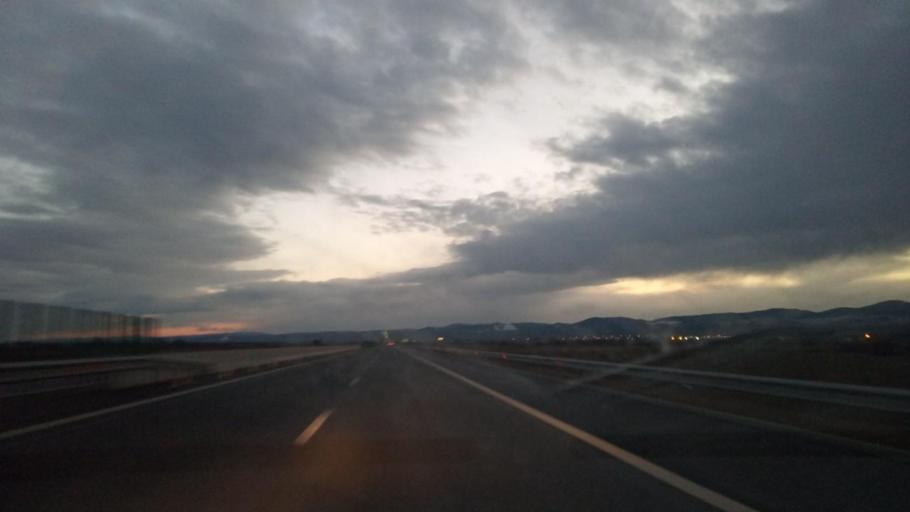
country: RO
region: Bacau
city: Ungureni
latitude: 46.5178
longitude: 26.9624
